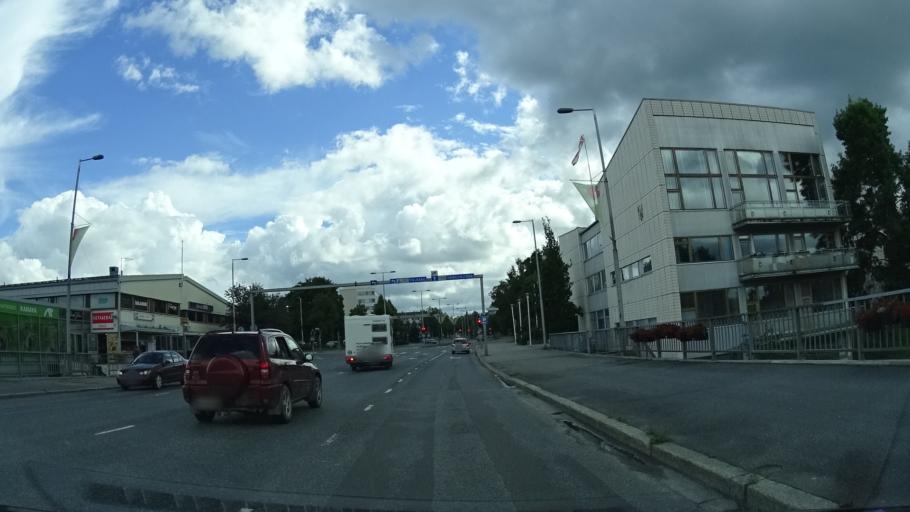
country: FI
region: Pirkanmaa
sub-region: Etelae-Pirkanmaa
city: Valkeakoski
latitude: 61.2647
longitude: 24.0310
